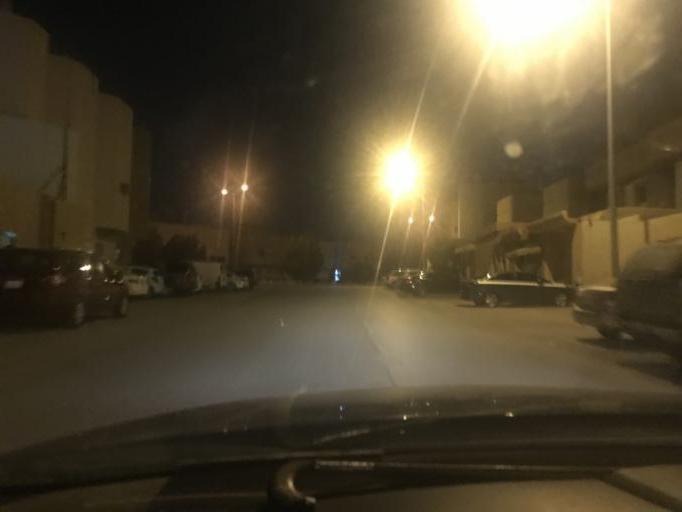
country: SA
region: Ar Riyad
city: Riyadh
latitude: 24.7585
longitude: 46.7616
